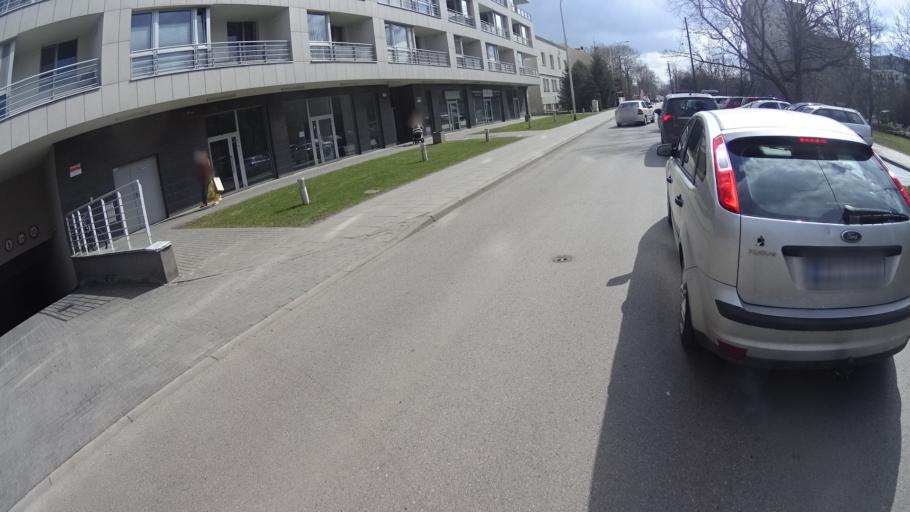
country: PL
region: Masovian Voivodeship
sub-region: Warszawa
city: Bemowo
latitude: 52.2233
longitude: 20.9368
